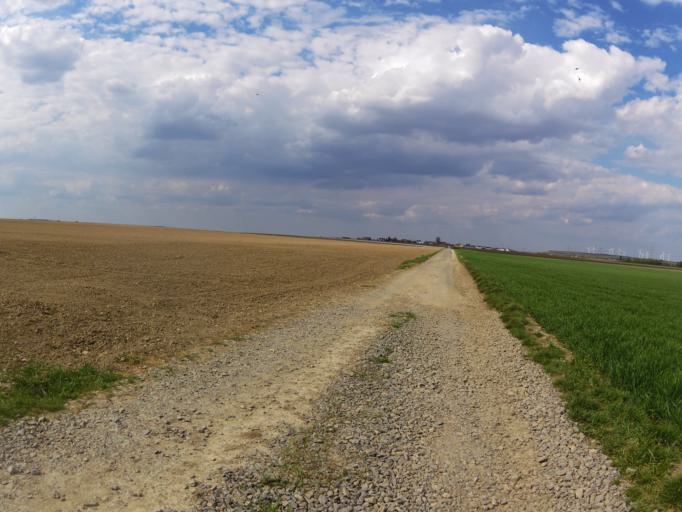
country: DE
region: Bavaria
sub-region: Regierungsbezirk Unterfranken
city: Oberpleichfeld
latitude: 49.8627
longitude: 10.0941
